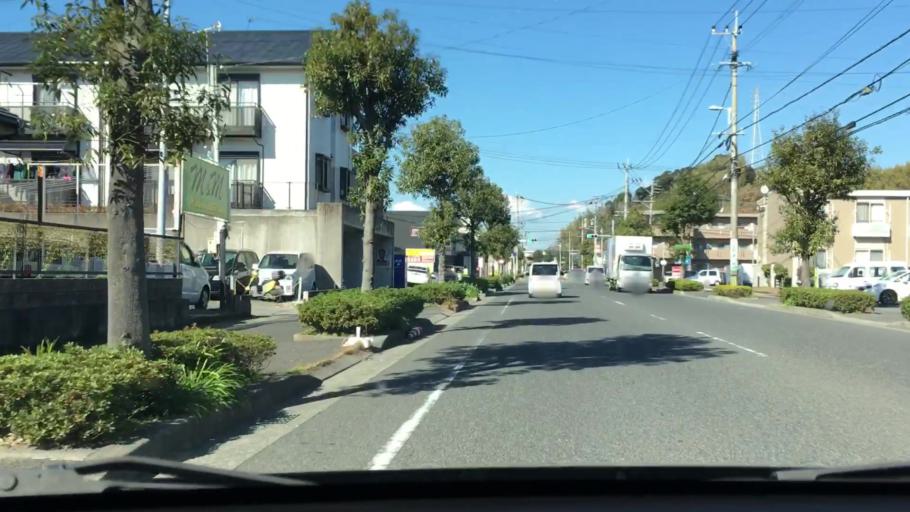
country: JP
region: Kagoshima
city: Kagoshima-shi
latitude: 31.5504
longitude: 130.5307
